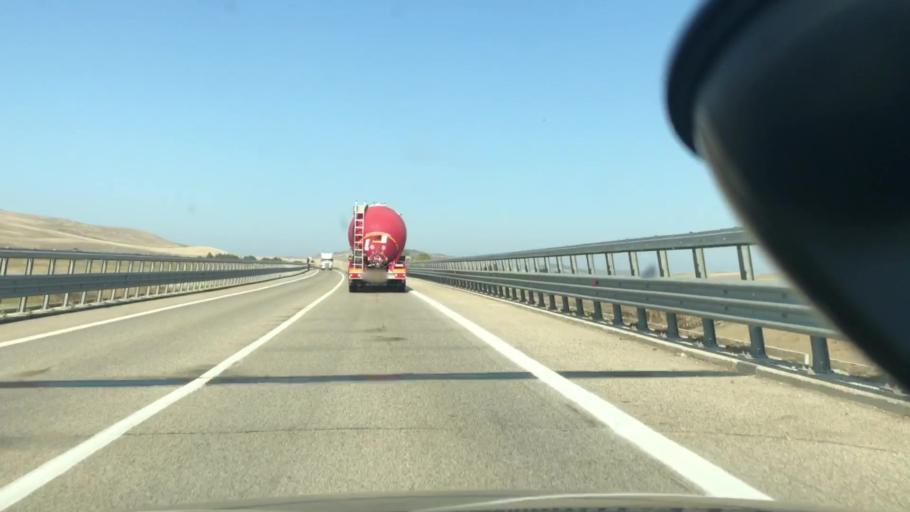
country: IT
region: Basilicate
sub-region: Provincia di Matera
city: Irsina
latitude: 40.7815
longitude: 16.3106
